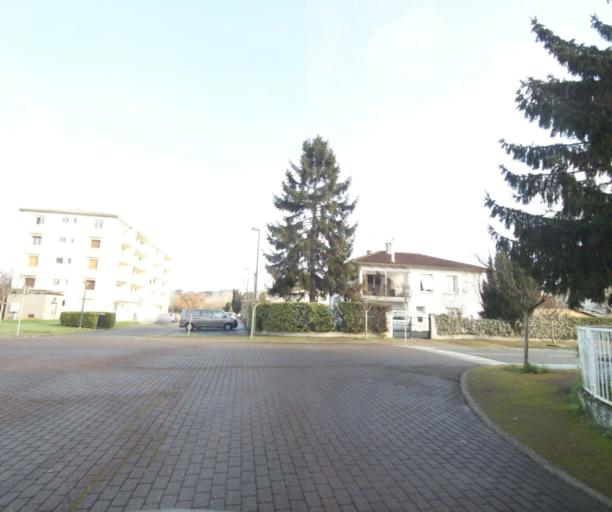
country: FR
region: Midi-Pyrenees
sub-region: Departement de la Haute-Garonne
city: Villemur-sur-Tarn
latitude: 43.8629
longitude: 1.4955
